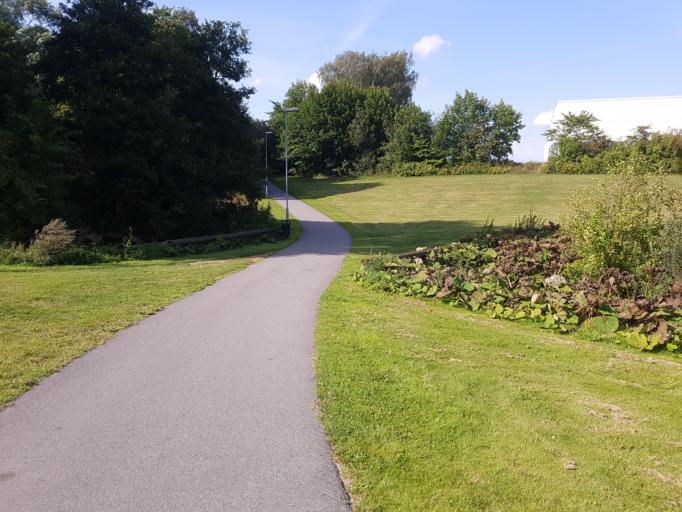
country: SE
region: Skane
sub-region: Sjobo Kommun
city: Sjoebo
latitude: 55.6358
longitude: 13.6998
